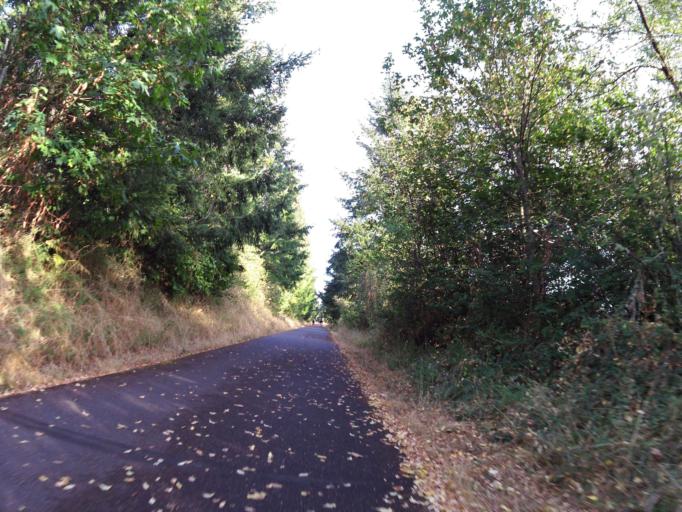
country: US
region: Washington
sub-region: Thurston County
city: Rainier
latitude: 46.8811
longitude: -122.7367
